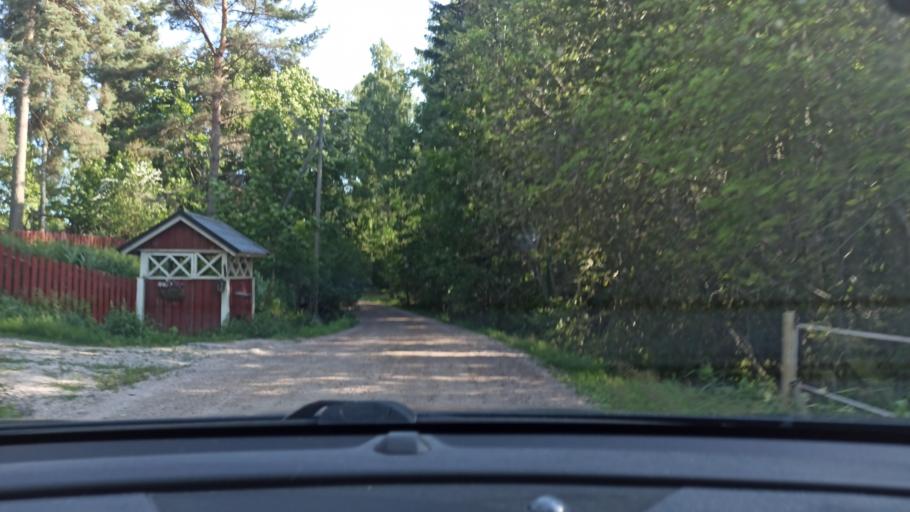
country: FI
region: Uusimaa
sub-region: Helsinki
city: Espoo
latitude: 60.2119
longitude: 24.5503
